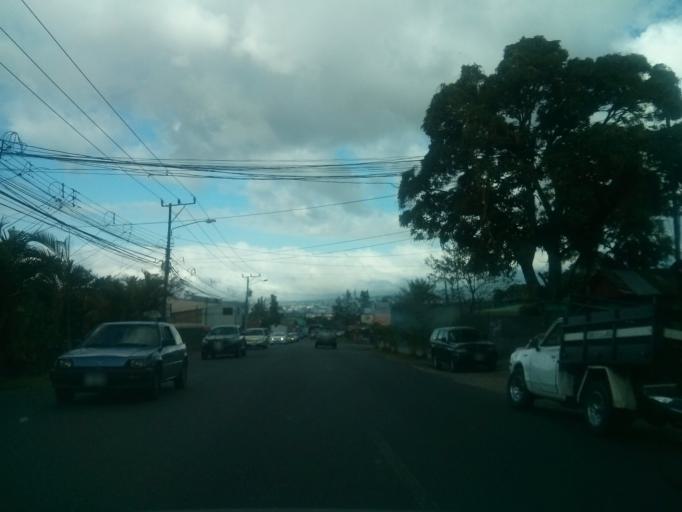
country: CR
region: San Jose
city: San Rafael Arriba
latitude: 9.8790
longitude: -84.0742
